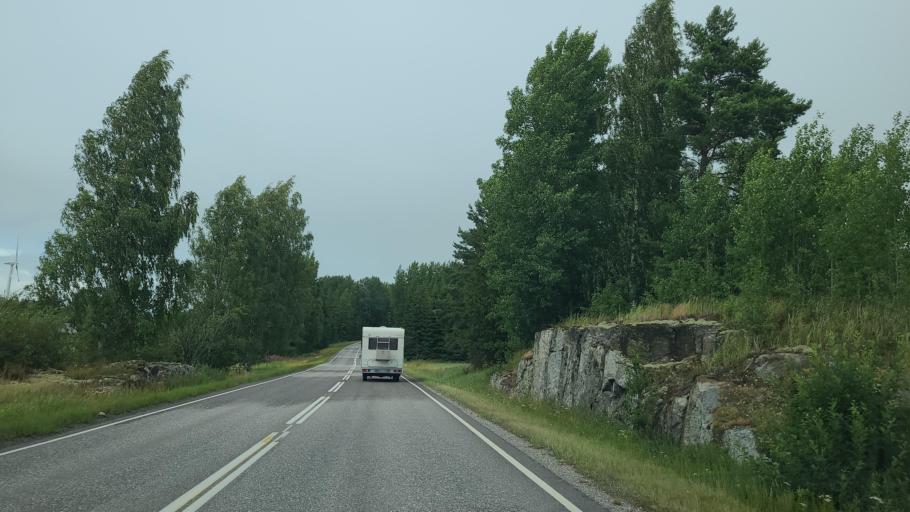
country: FI
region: Varsinais-Suomi
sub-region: Turku
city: Sauvo
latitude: 60.2994
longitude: 22.6800
